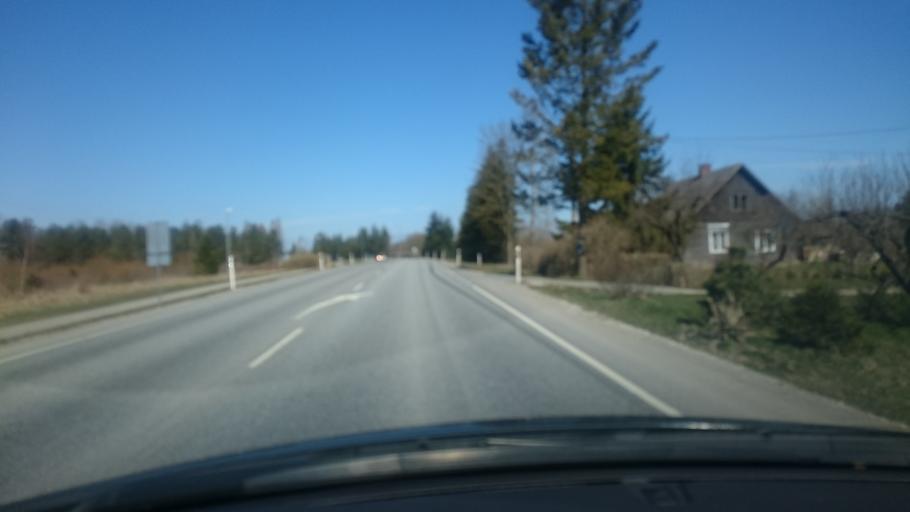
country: EE
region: Raplamaa
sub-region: Rapla vald
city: Rapla
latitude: 58.9858
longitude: 24.8415
